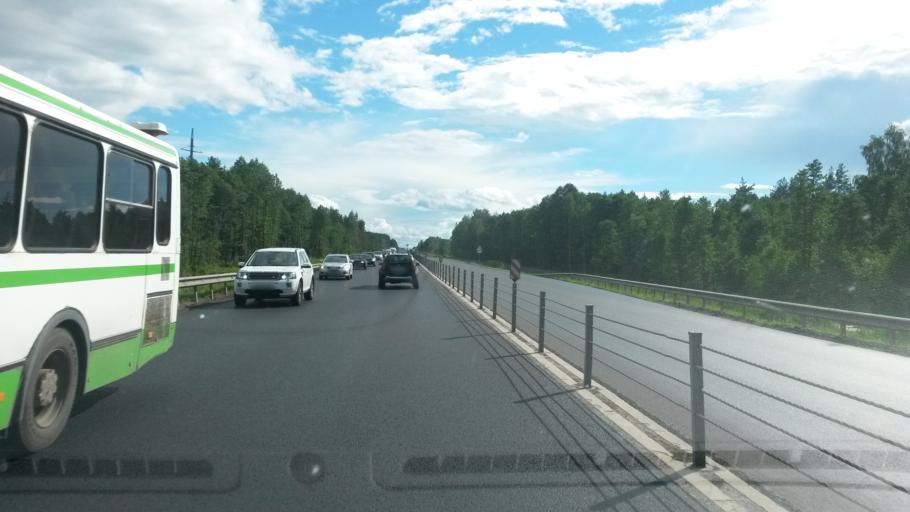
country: RU
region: Jaroslavl
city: Semibratovo
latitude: 57.2561
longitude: 39.4863
